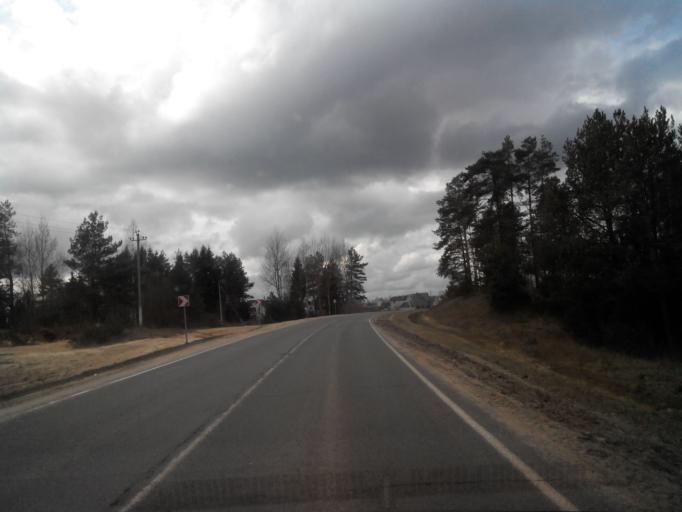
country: BY
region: Vitebsk
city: Pastavy
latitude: 55.0950
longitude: 26.8444
